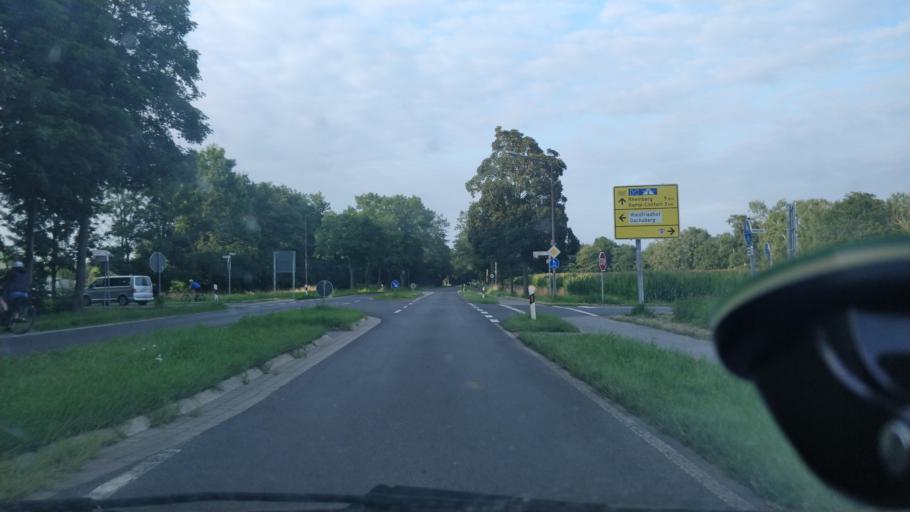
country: DE
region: North Rhine-Westphalia
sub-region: Regierungsbezirk Dusseldorf
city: Kamp-Lintfort
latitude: 51.4954
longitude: 6.5075
